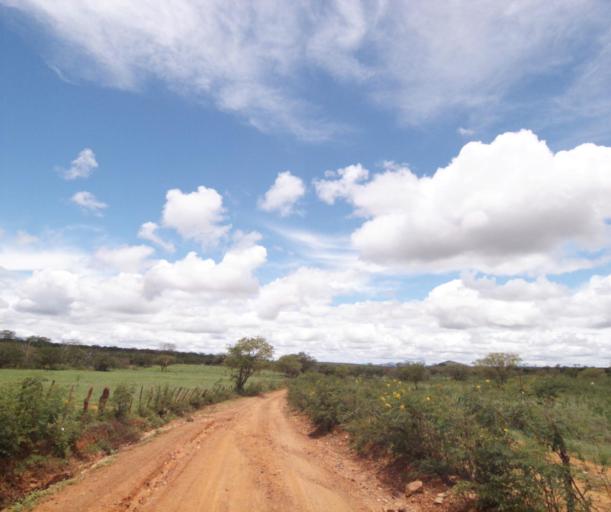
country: BR
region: Bahia
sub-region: Tanhacu
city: Tanhacu
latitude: -14.1843
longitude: -41.0892
